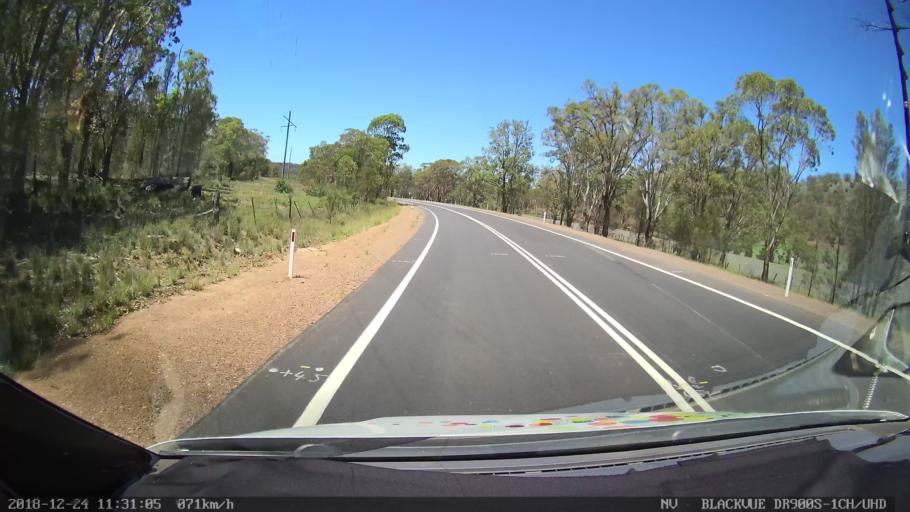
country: AU
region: New South Wales
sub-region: Upper Hunter Shire
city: Merriwa
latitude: -32.2113
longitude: 150.4615
